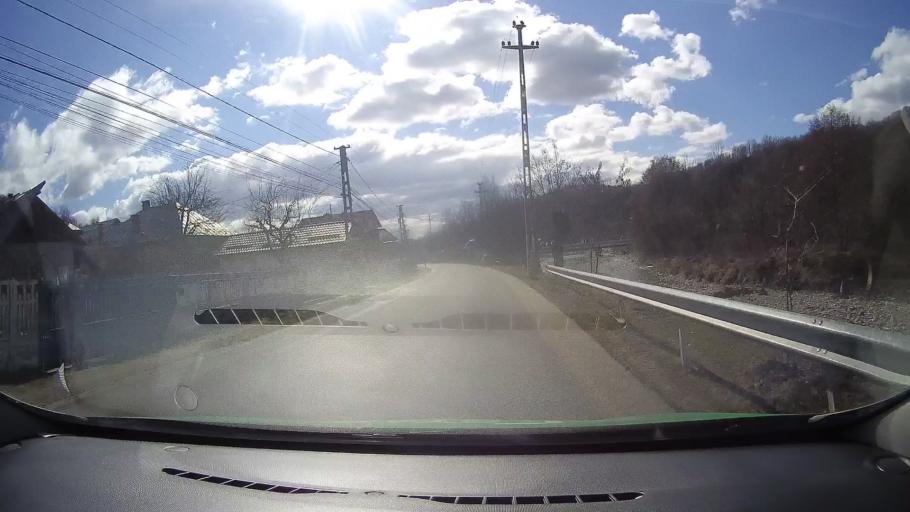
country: RO
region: Dambovita
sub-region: Comuna Runcu
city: Badeni
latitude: 45.1552
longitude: 25.3996
